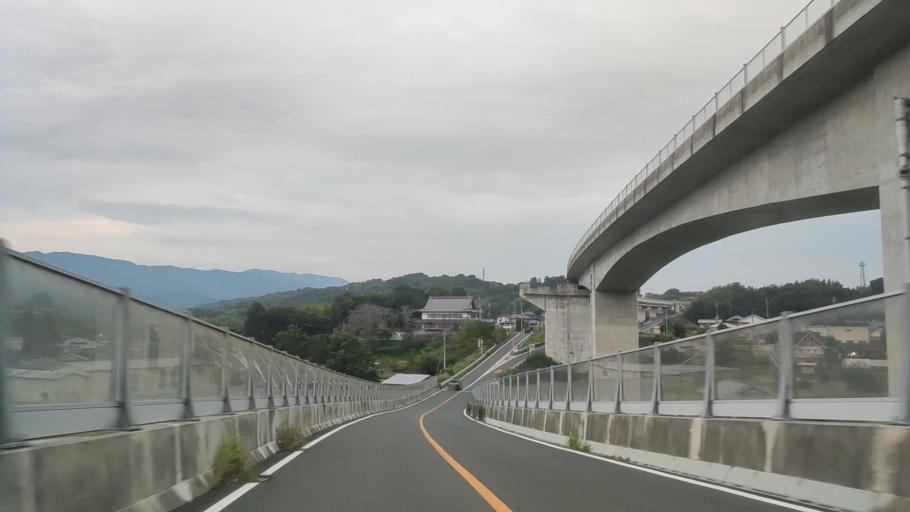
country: JP
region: Wakayama
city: Hashimoto
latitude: 34.3247
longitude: 135.6074
